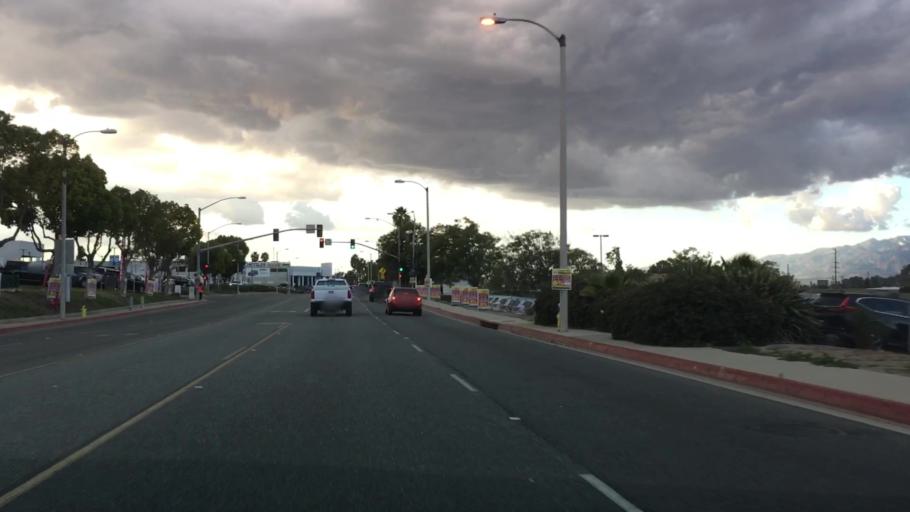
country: US
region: California
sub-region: Los Angeles County
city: South San Jose Hills
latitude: 33.9982
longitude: -117.9271
